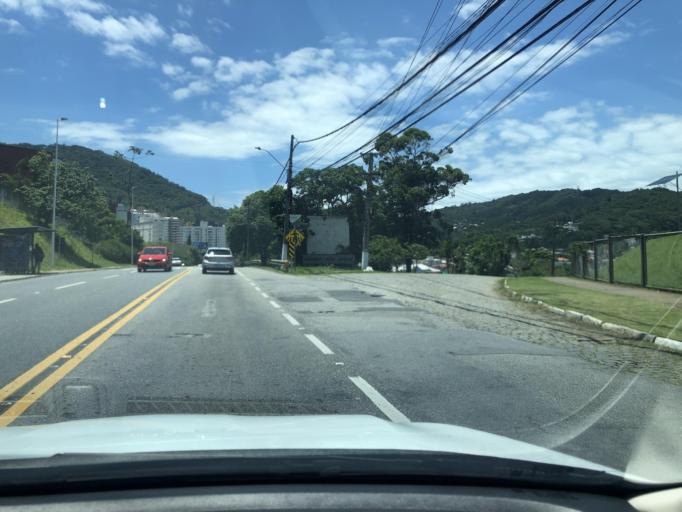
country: BR
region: Santa Catarina
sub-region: Florianopolis
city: Itacorubi
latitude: -27.5879
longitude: -48.4976
